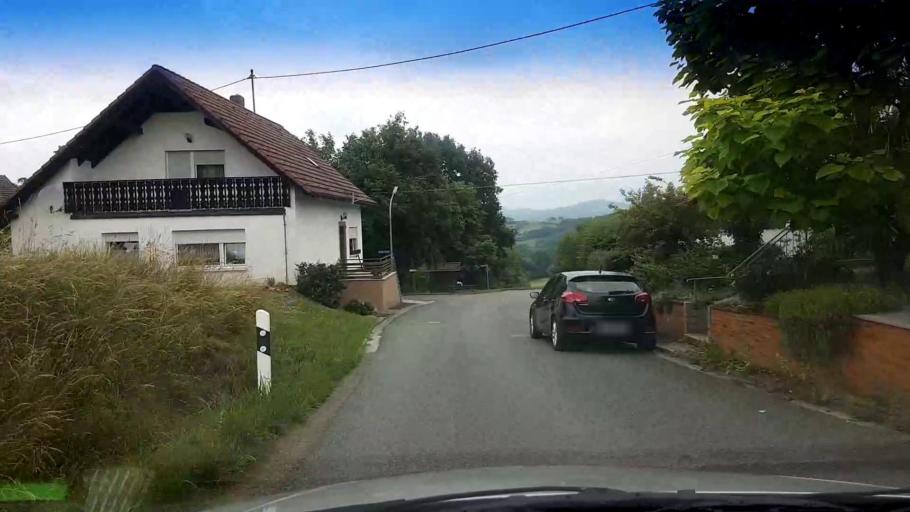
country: DE
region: Bavaria
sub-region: Upper Franconia
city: Mainleus
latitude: 50.0789
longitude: 11.3387
